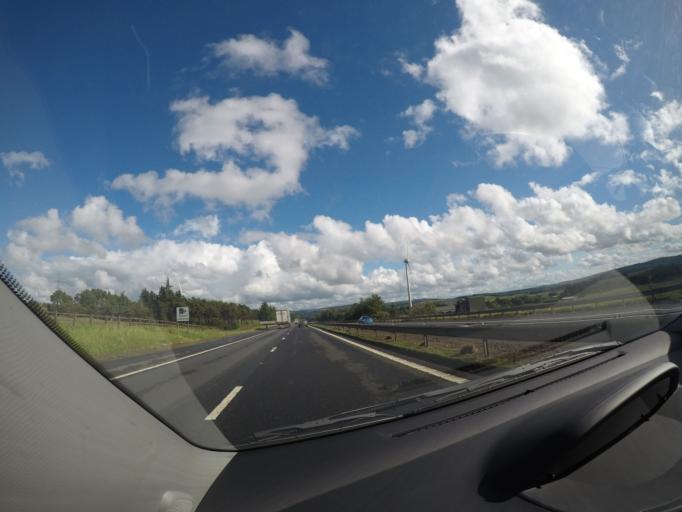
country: GB
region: Scotland
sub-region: South Lanarkshire
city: Lesmahagow
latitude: 55.6072
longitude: -3.8421
